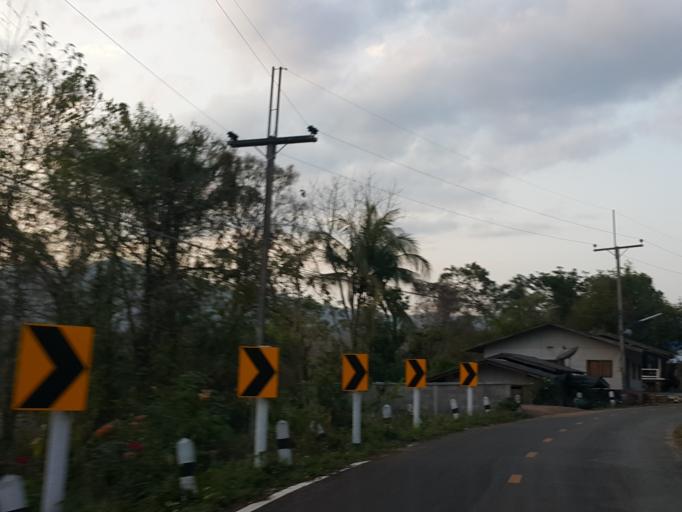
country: TH
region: Lampang
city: Mueang Pan
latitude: 18.7924
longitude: 99.4916
